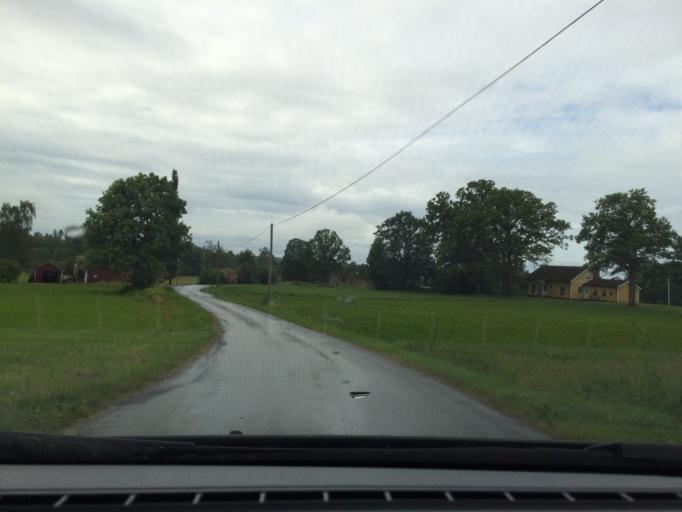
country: SE
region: Joenkoeping
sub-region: Varnamo Kommun
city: Varnamo
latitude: 57.1883
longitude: 13.9412
